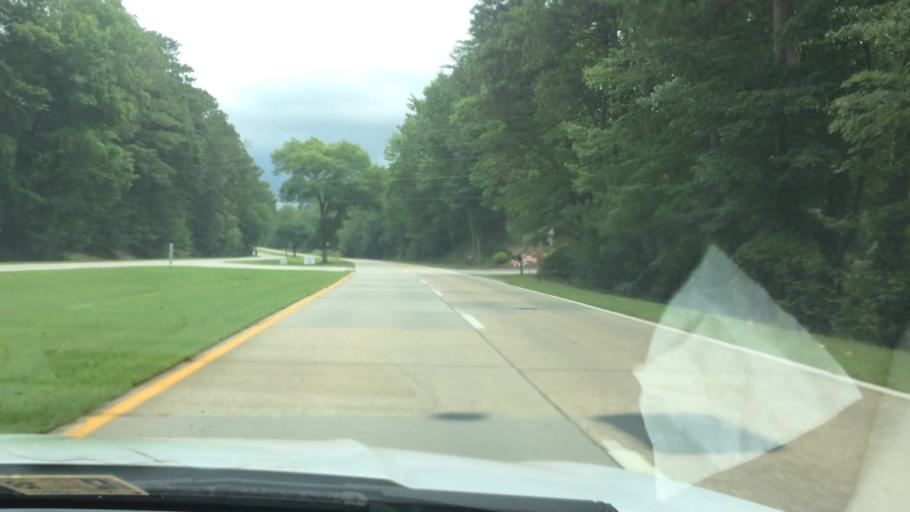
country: US
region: Virginia
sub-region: King William County
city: West Point
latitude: 37.4058
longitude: -76.8506
